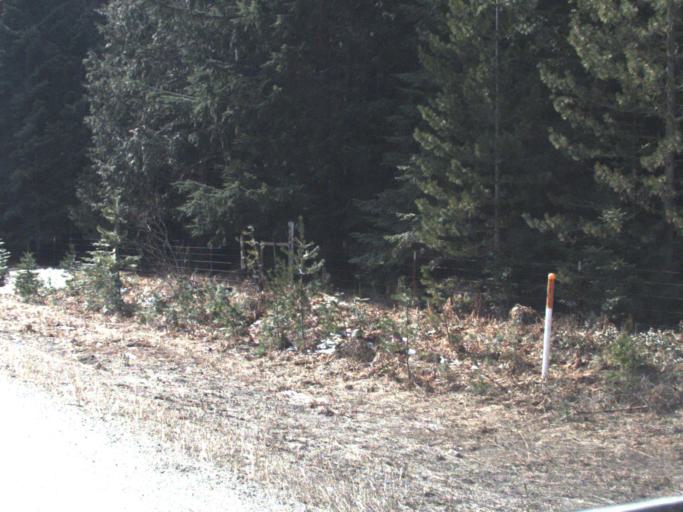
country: CA
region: British Columbia
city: Fruitvale
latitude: 48.6698
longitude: -117.3981
